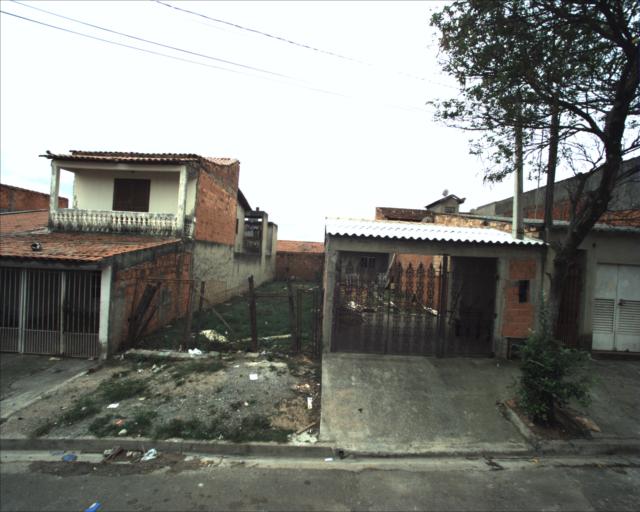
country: BR
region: Sao Paulo
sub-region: Sorocaba
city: Sorocaba
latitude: -23.4353
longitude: -47.5104
